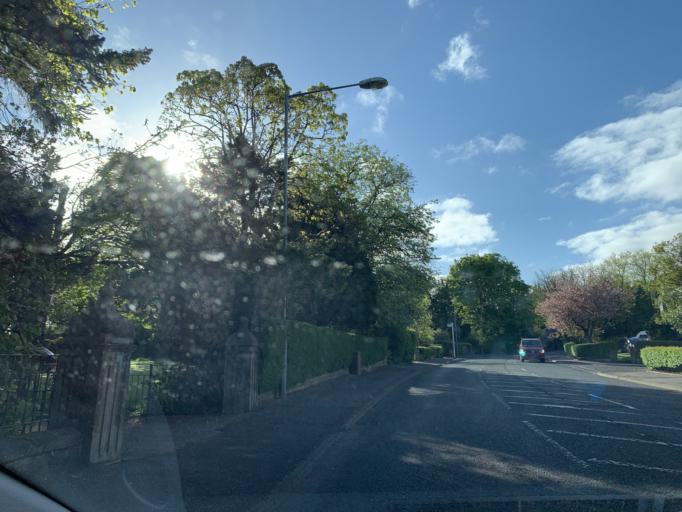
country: GB
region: Scotland
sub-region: East Renfrewshire
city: Busby
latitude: 55.7793
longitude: -4.2561
